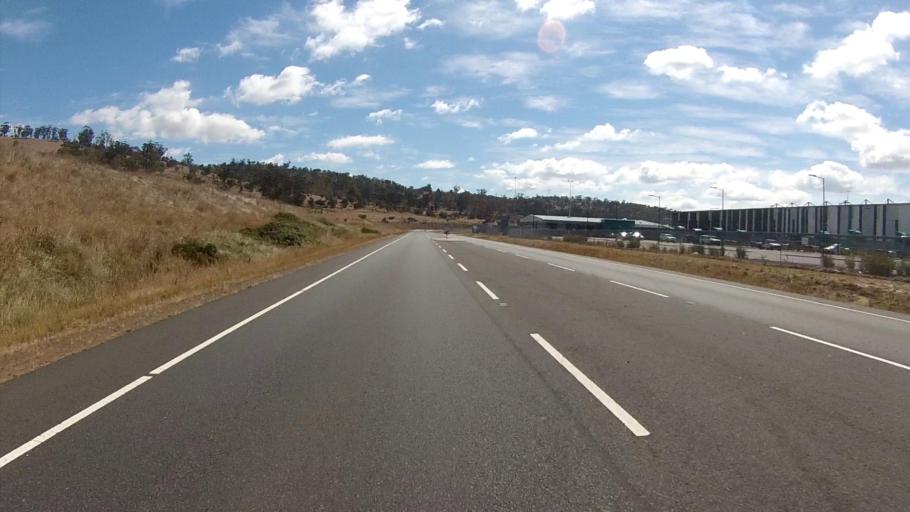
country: AU
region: Tasmania
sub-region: Brighton
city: Bridgewater
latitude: -42.7162
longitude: 147.2264
